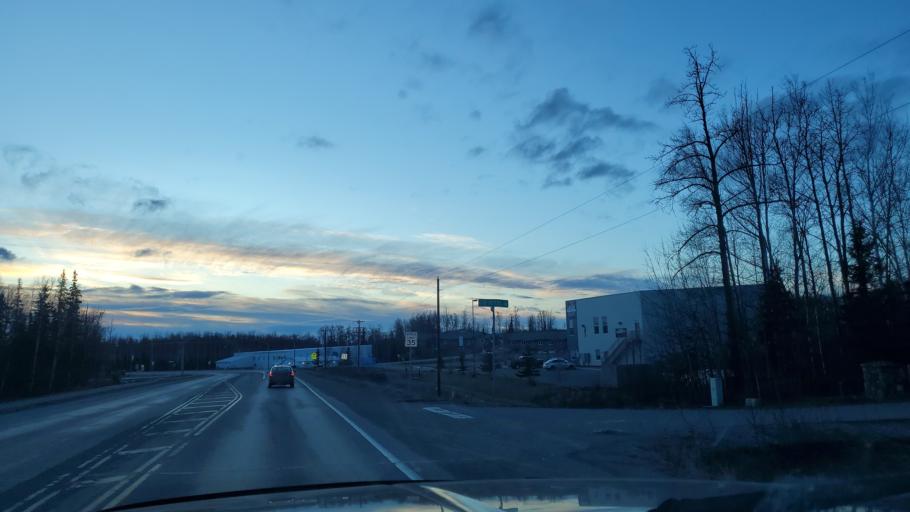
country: US
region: Alaska
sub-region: Matanuska-Susitna Borough
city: Wasilla
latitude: 61.5907
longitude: -149.4404
